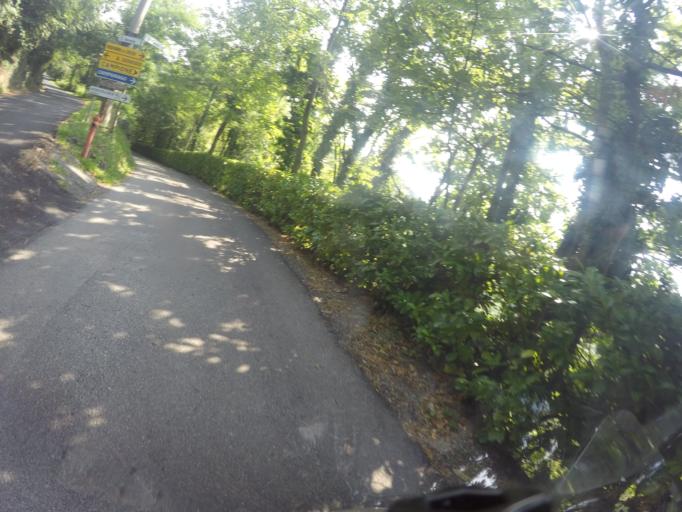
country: IT
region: Lombardy
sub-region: Provincia di Lecco
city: Santa Maria Hoe
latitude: 45.7522
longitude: 9.3907
